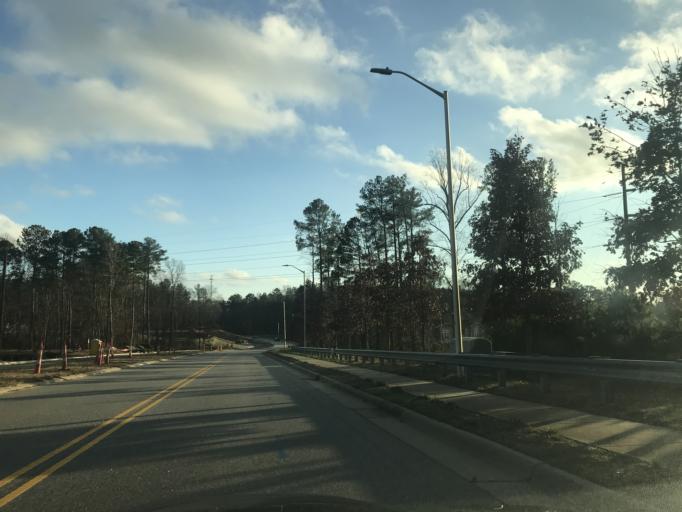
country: US
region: North Carolina
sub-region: Wake County
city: Wake Forest
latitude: 35.9590
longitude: -78.5339
